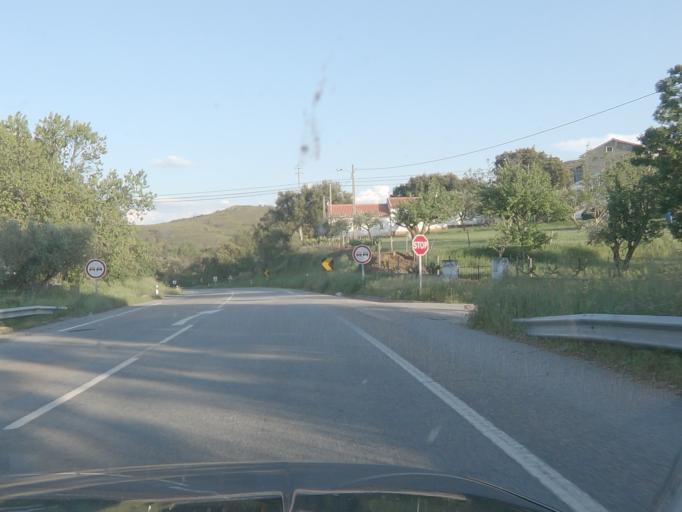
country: PT
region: Portalegre
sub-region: Portalegre
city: Sao Juliao
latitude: 39.3650
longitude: -7.3354
